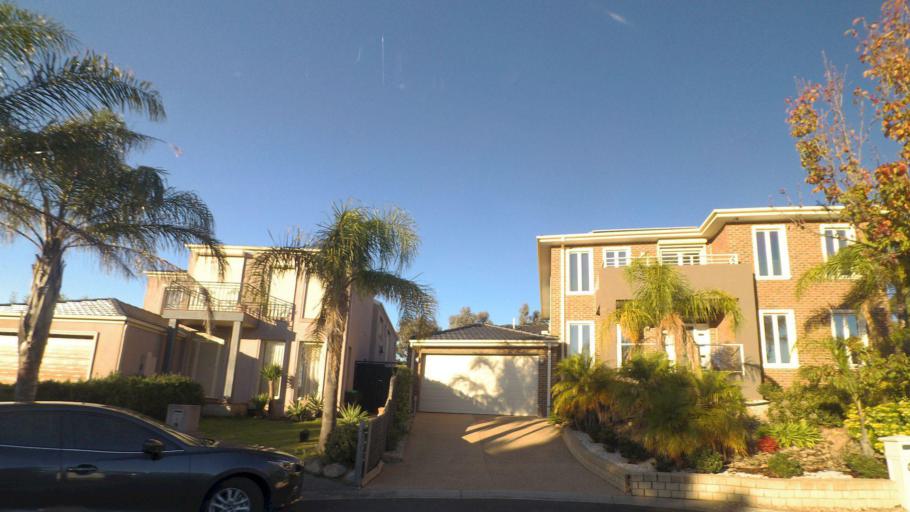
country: AU
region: Victoria
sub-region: Banyule
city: Greensborough
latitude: -37.6870
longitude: 145.1075
